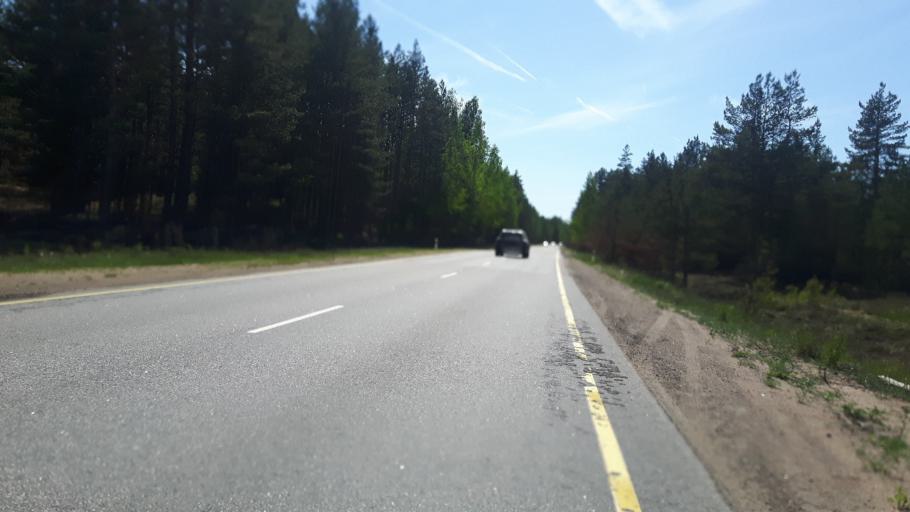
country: RU
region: Leningrad
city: Sista-Palkino
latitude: 59.7791
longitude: 28.8681
